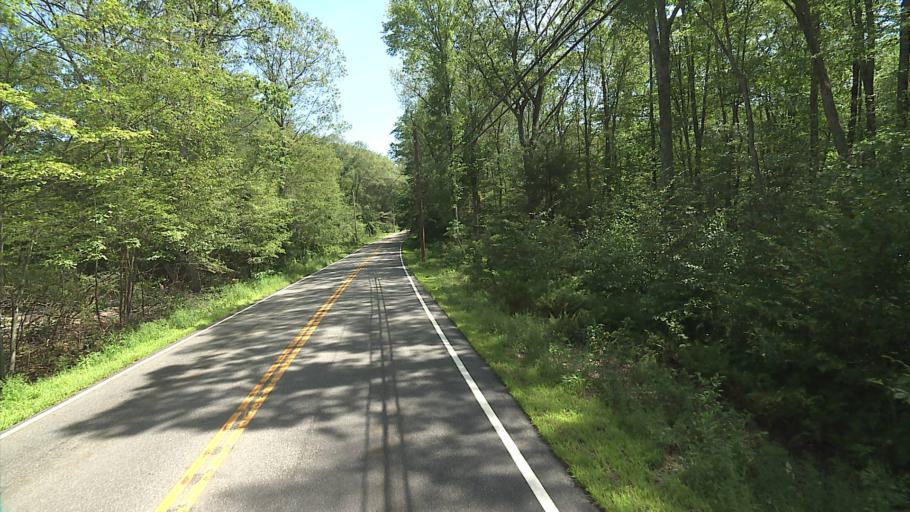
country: US
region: Connecticut
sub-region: Windham County
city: South Woodstock
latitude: 41.8964
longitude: -72.0494
